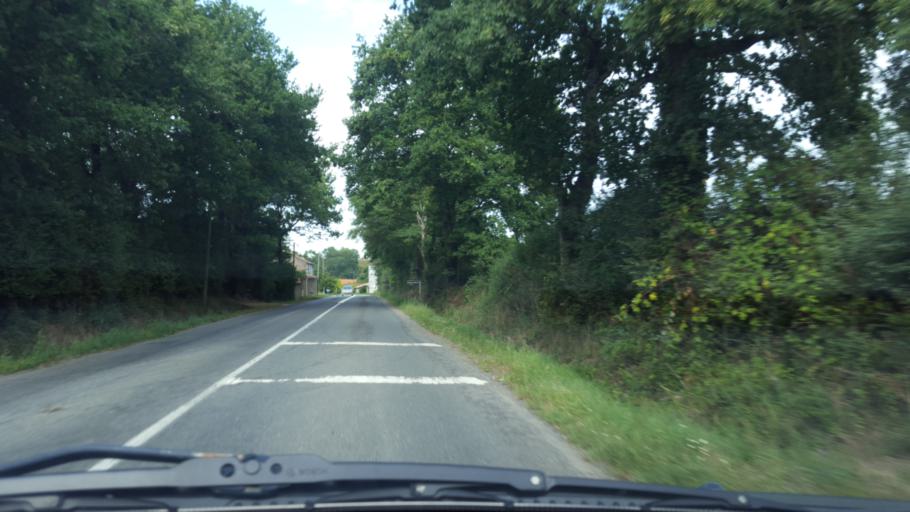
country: FR
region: Pays de la Loire
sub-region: Departement de la Loire-Atlantique
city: Touvois
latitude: 46.9694
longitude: -1.6739
